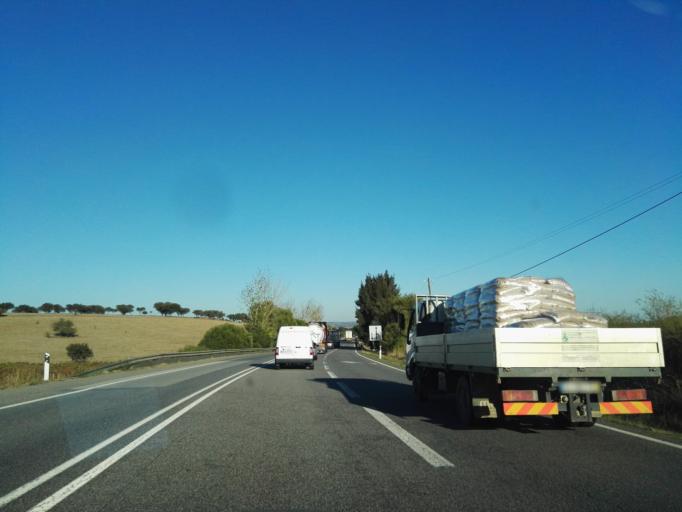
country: PT
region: Evora
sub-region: Borba
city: Borba
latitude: 38.8247
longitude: -7.4217
